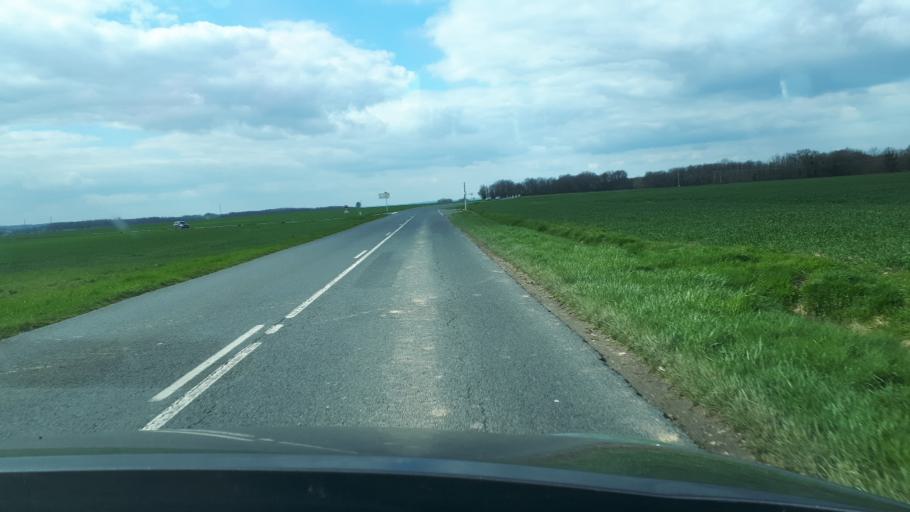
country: FR
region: Centre
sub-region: Departement du Loir-et-Cher
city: Lunay
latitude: 47.7617
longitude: 0.9483
